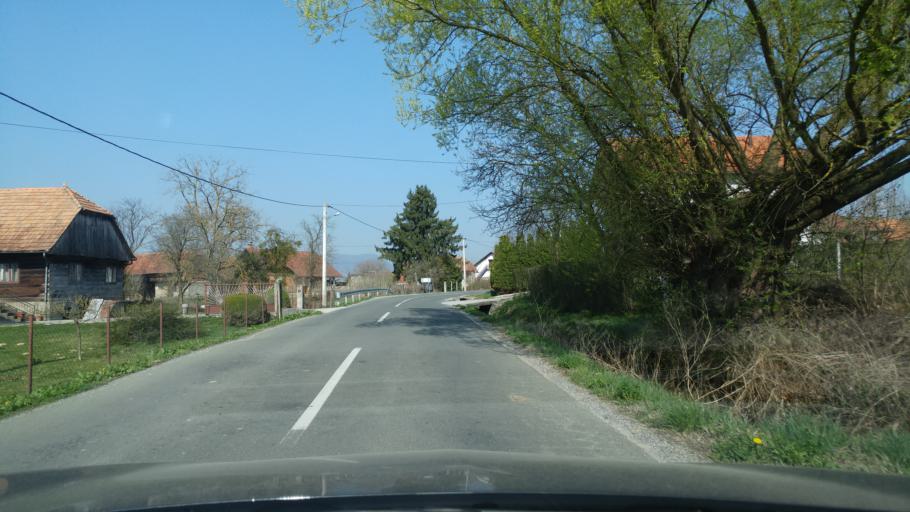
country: SI
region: Bistrica ob Sotli
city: Bistrica ob Sotli
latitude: 45.9812
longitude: 15.7290
